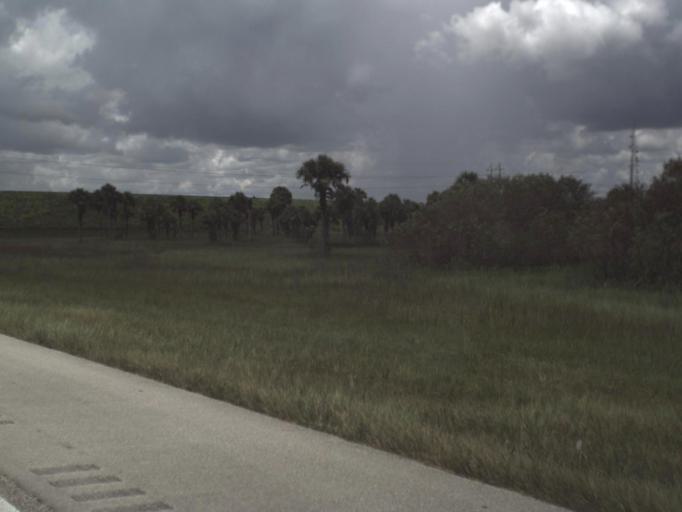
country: US
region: Florida
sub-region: Collier County
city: Immokalee
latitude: 26.1549
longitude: -81.3432
